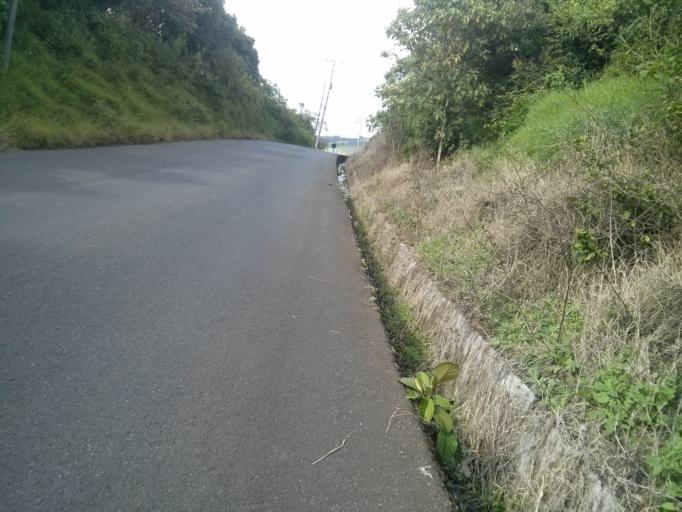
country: CR
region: Cartago
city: Cartago
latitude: 9.8985
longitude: -83.9407
